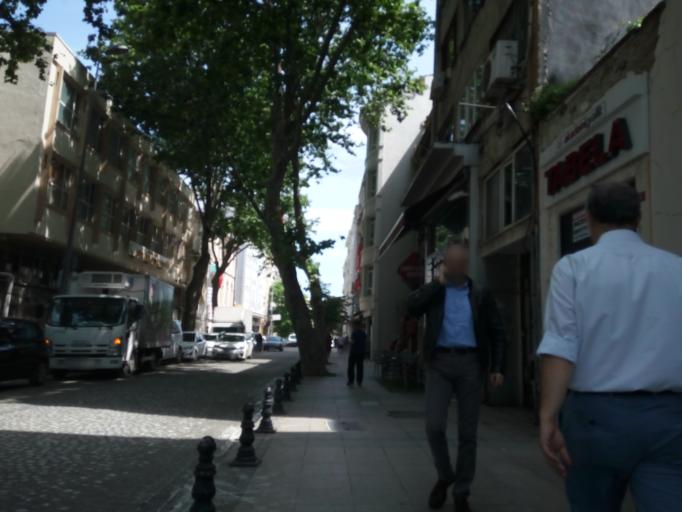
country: TR
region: Istanbul
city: Eminoenue
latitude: 41.0087
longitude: 28.9735
